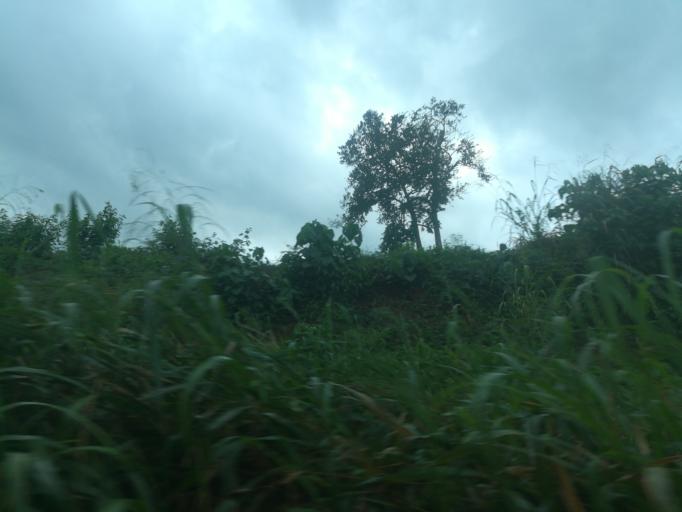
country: NG
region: Lagos
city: Ikorodu
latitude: 6.6642
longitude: 3.6063
